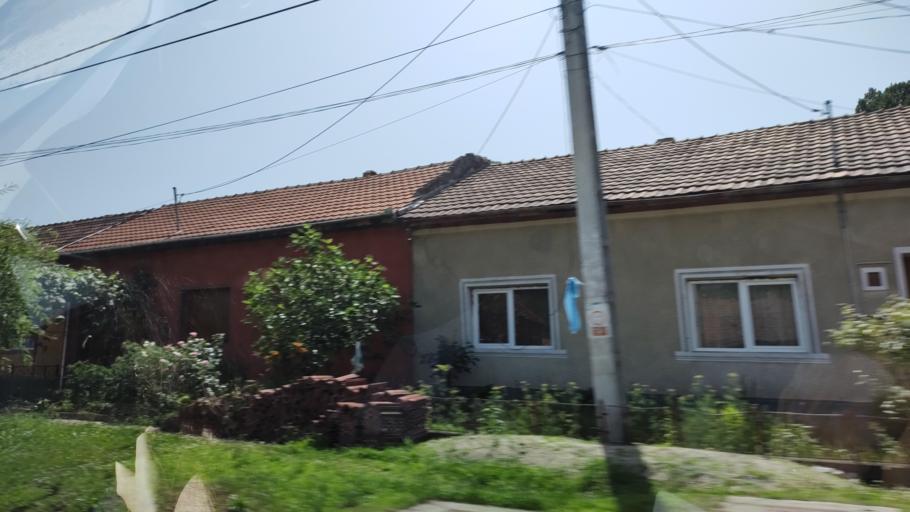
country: RO
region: Mehedinti
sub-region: Comuna Eselnita
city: Eselnita
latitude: 44.7059
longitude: 22.3601
